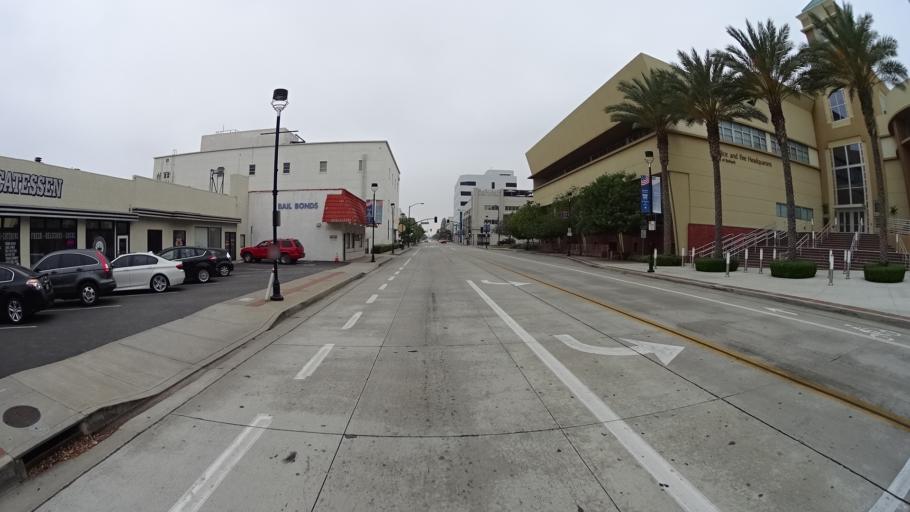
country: US
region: California
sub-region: Los Angeles County
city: Burbank
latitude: 34.1828
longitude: -118.3087
